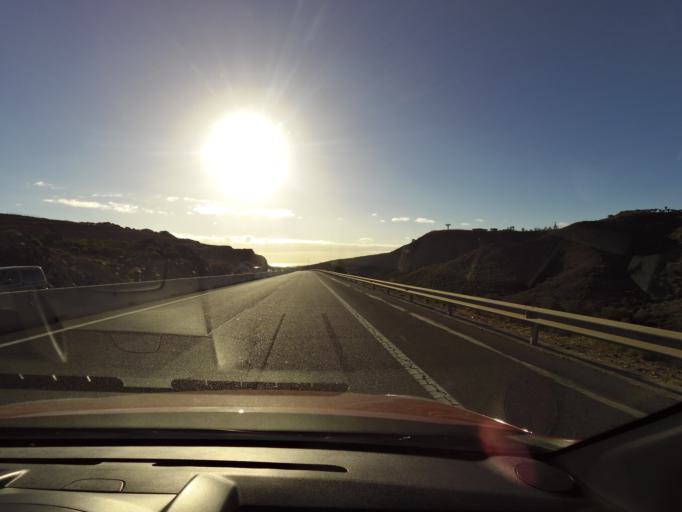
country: ES
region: Canary Islands
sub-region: Provincia de Las Palmas
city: Maspalomas
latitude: 27.7686
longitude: -15.6332
